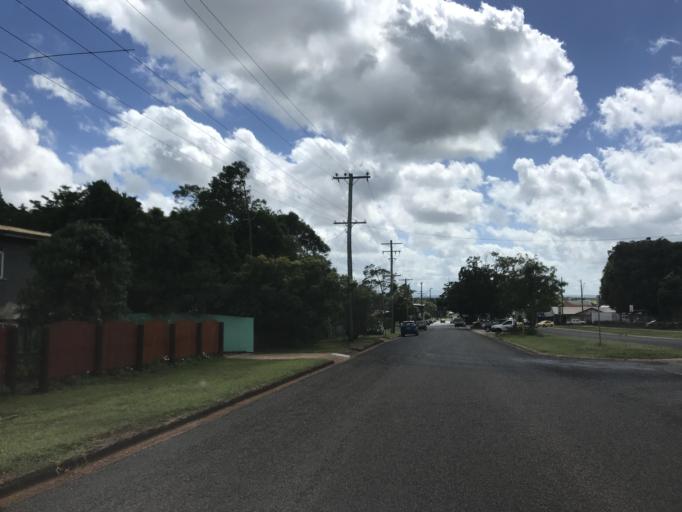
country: AU
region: Queensland
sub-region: Tablelands
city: Tolga
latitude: -17.2229
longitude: 145.4774
